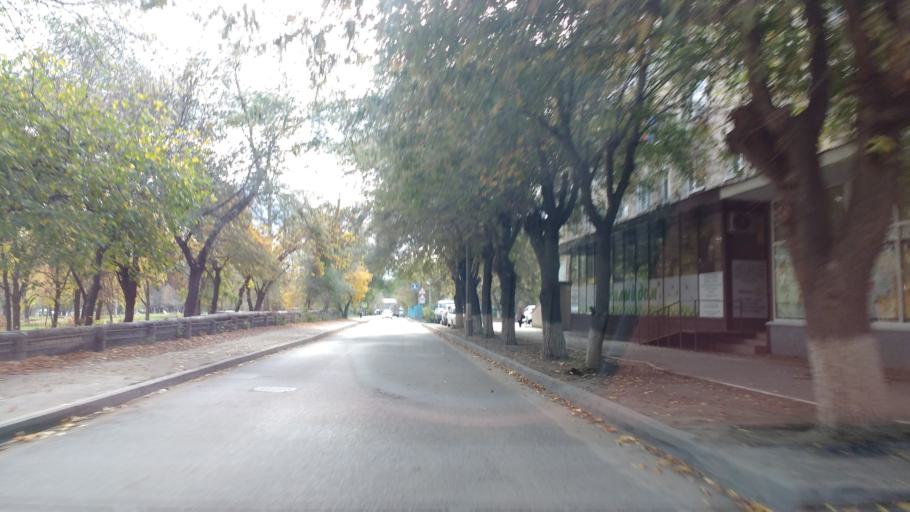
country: RU
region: Volgograd
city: Krasnoslobodsk
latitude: 48.7556
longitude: 44.5513
